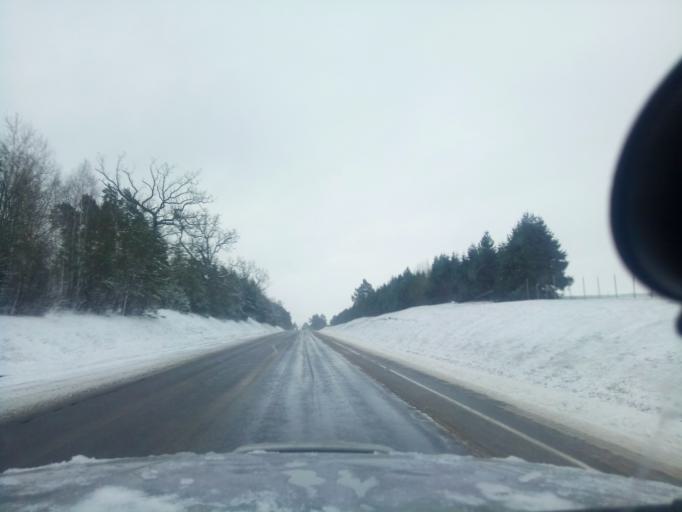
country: BY
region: Minsk
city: Nyasvizh
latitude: 53.2624
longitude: 26.6089
